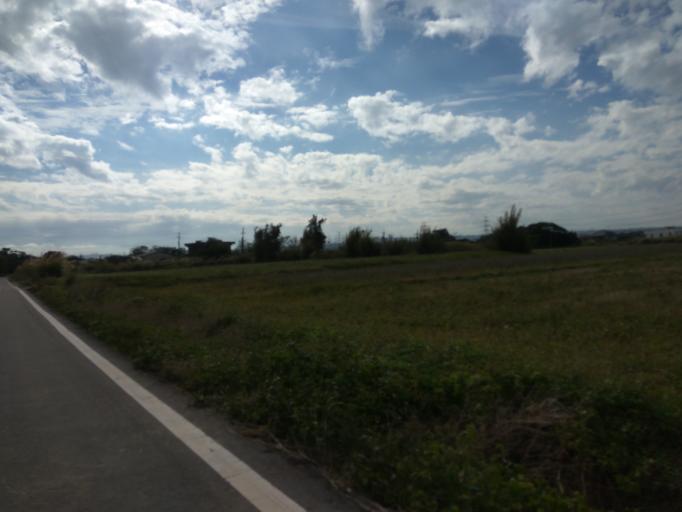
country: TW
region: Taiwan
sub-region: Hsinchu
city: Zhubei
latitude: 24.9582
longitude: 121.1048
